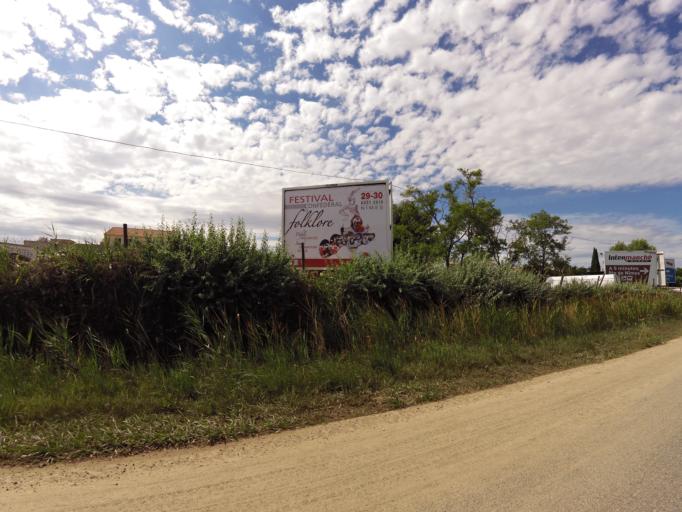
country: FR
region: Languedoc-Roussillon
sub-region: Departement du Gard
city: Le Grau-du-Roi
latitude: 43.5288
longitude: 4.1504
